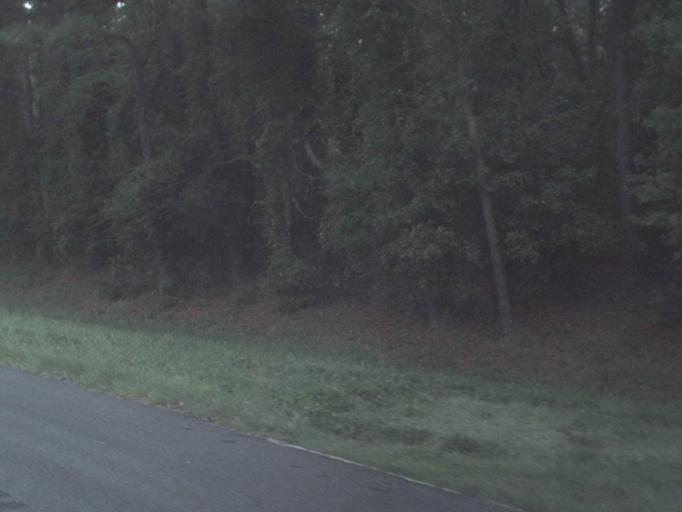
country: US
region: Florida
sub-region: Columbia County
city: Lake City
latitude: 30.0366
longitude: -82.6163
